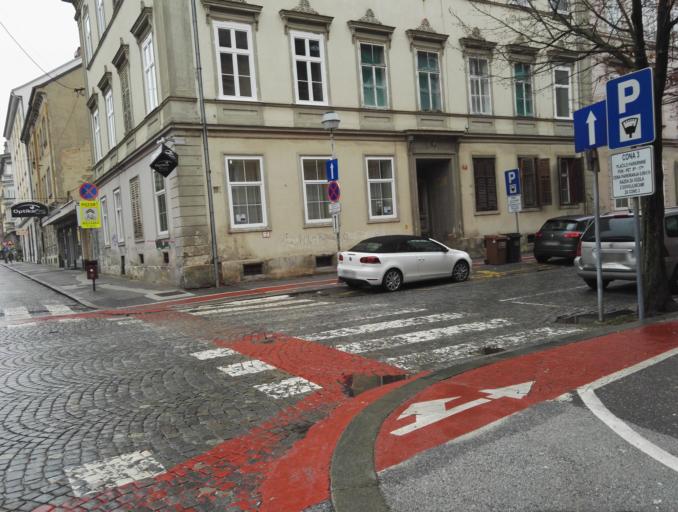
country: SI
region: Maribor
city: Maribor
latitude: 46.5612
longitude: 15.6467
